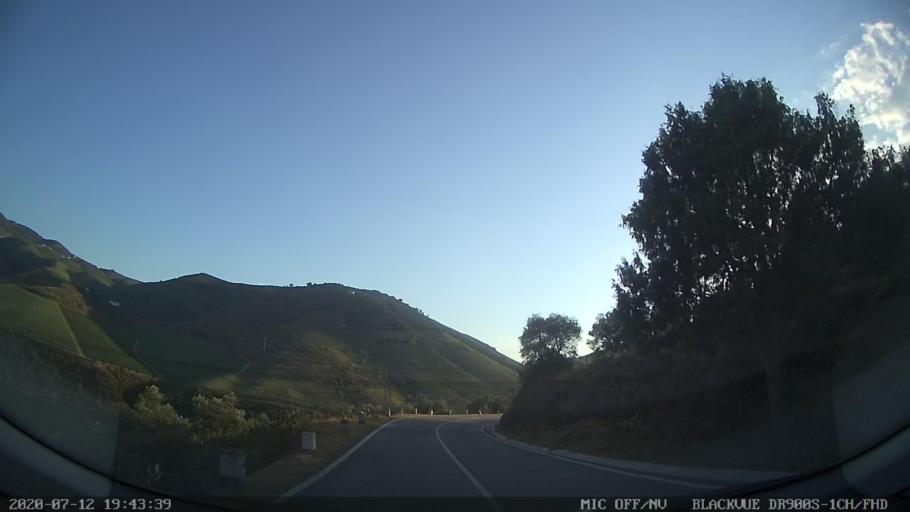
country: PT
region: Viseu
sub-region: Sao Joao da Pesqueira
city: Sao Joao da Pesqueira
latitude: 41.2141
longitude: -7.4333
